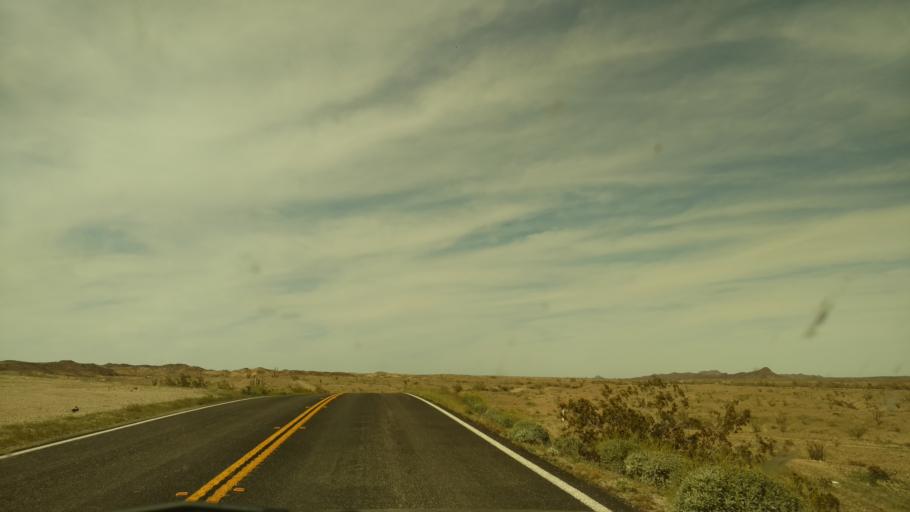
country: MX
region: Baja California
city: Los Algodones
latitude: 33.0992
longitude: -114.9013
